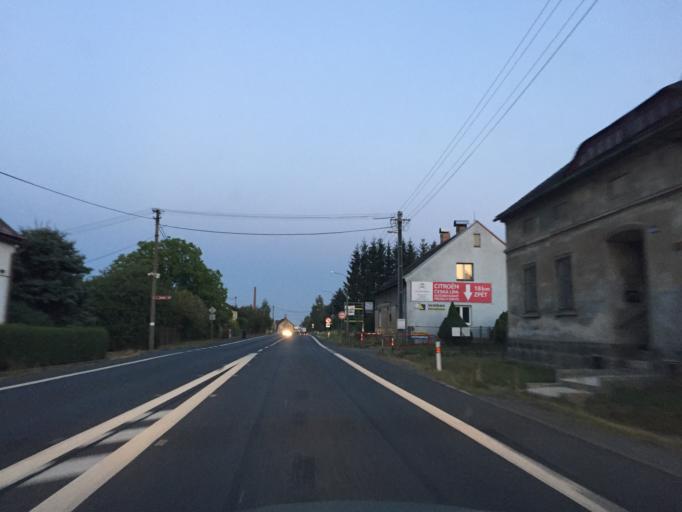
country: CZ
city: Cvikov
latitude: 50.7828
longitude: 14.6173
